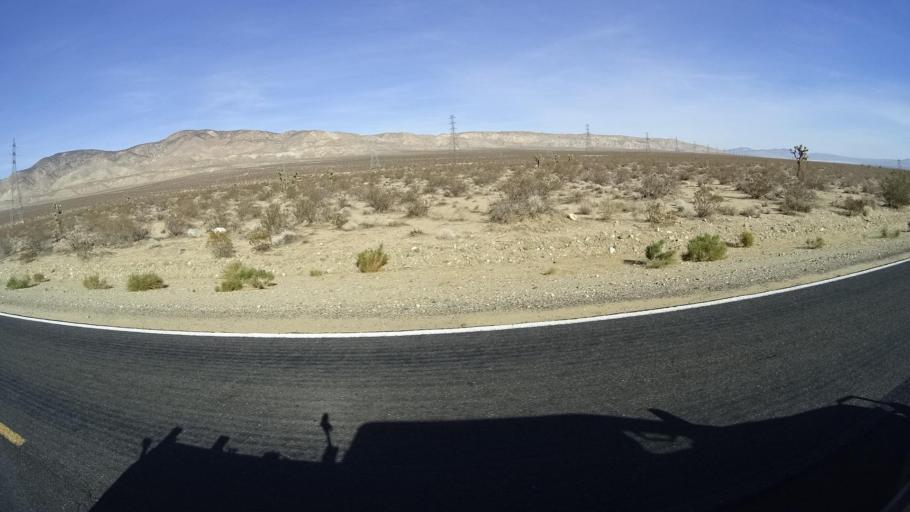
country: US
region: California
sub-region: Kern County
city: Mojave
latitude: 35.1242
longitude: -118.1543
